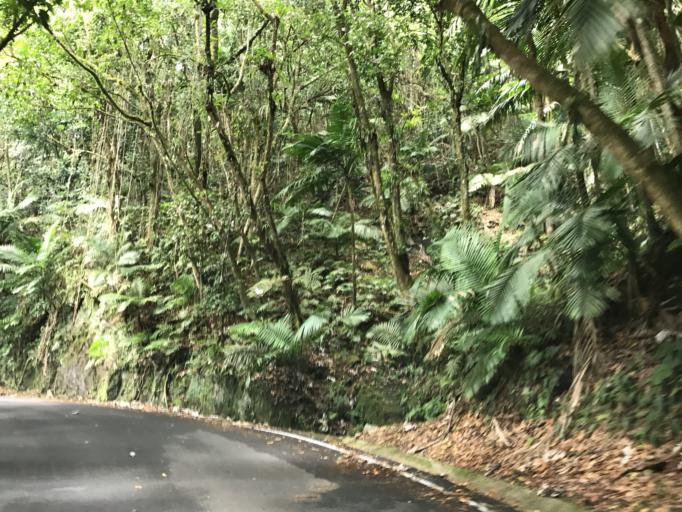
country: PR
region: Rio Grande
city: Palmer
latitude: 18.3150
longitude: -65.7713
